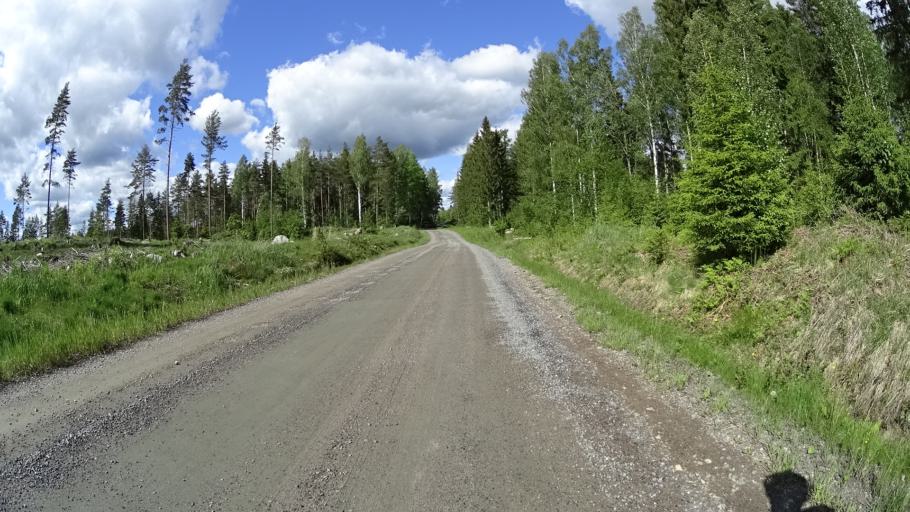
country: FI
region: Uusimaa
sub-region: Raaseporin
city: Pohja
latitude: 60.1773
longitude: 23.5873
